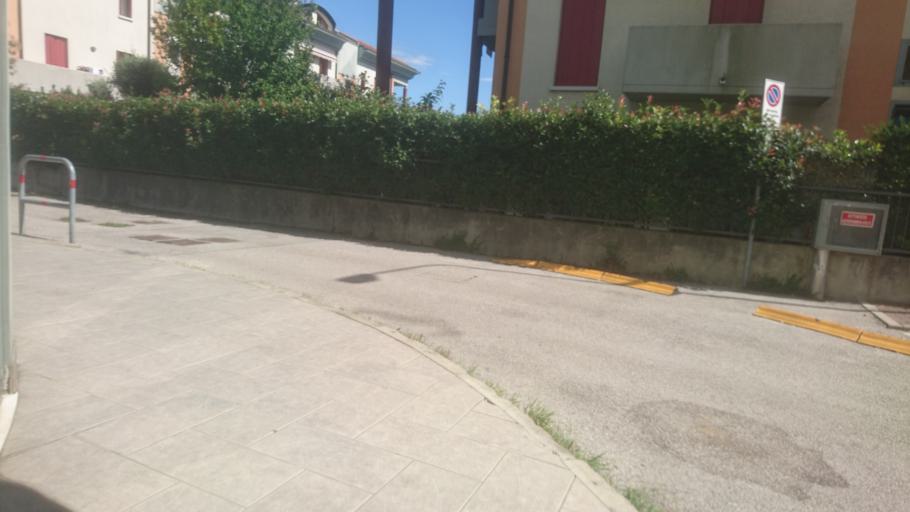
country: IT
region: Veneto
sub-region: Provincia di Venezia
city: Mira Taglio
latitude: 45.4328
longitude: 12.1342
